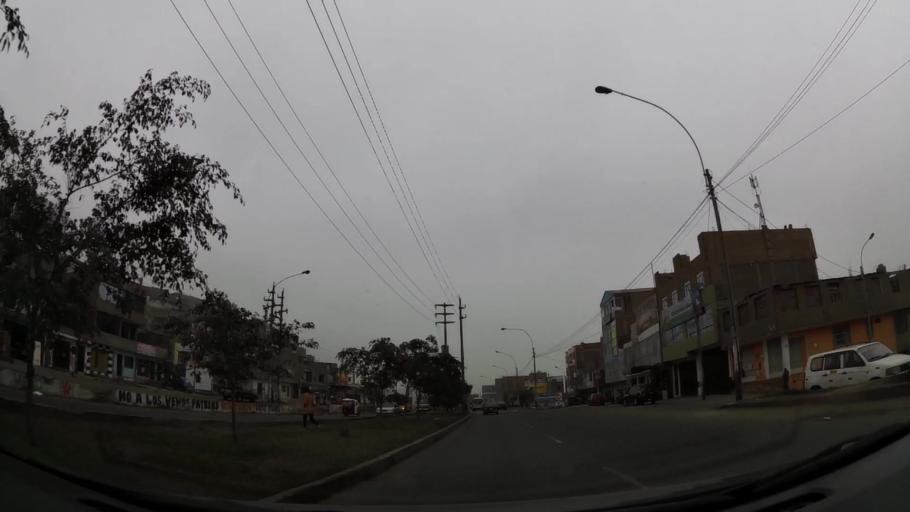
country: PE
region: Lima
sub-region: Lima
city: Urb. Santo Domingo
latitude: -11.8921
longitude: -77.0277
